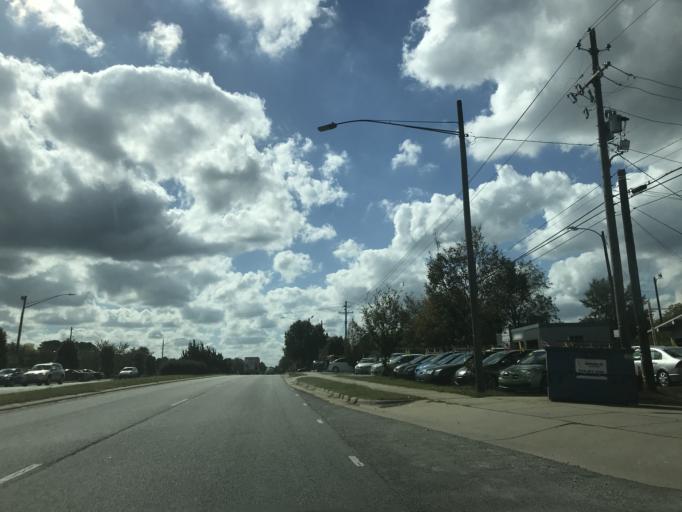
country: US
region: North Carolina
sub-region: Wake County
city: Raleigh
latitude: 35.7480
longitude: -78.6440
